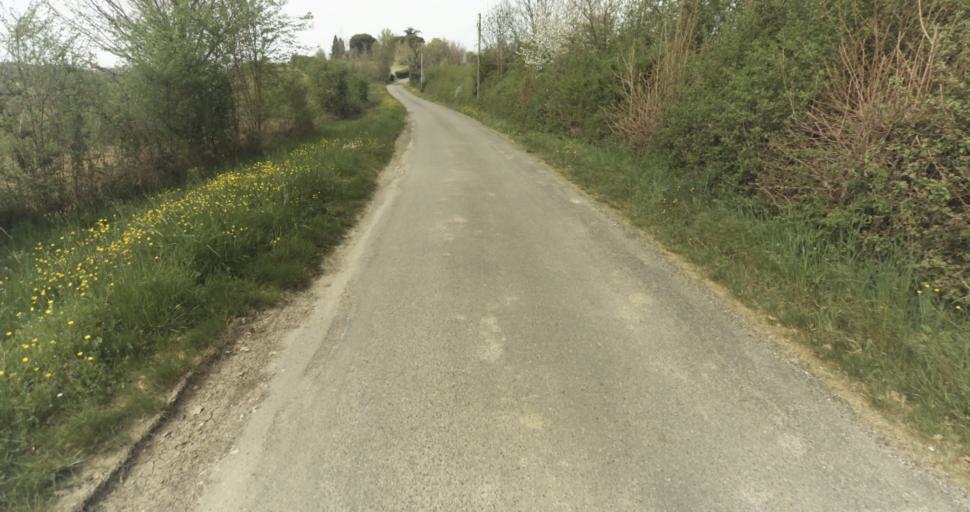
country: FR
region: Midi-Pyrenees
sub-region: Departement du Tarn-et-Garonne
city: Moissac
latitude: 44.1272
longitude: 1.1116
